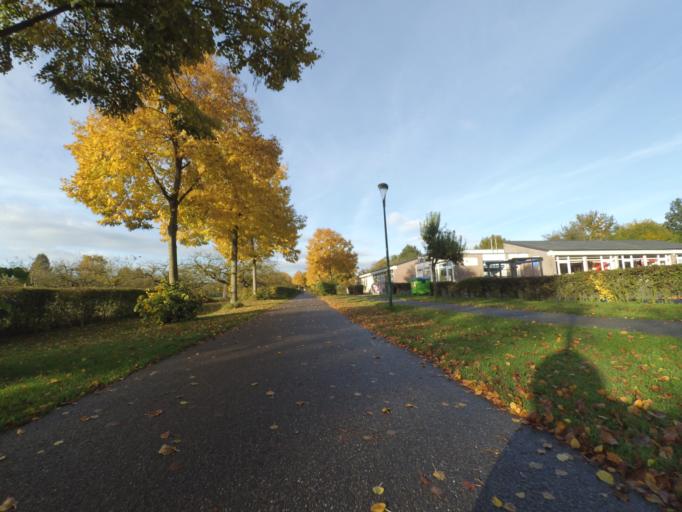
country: NL
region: Utrecht
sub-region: Gemeente Wijk bij Duurstede
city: Wijk bij Duurstede
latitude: 51.9759
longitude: 5.3334
